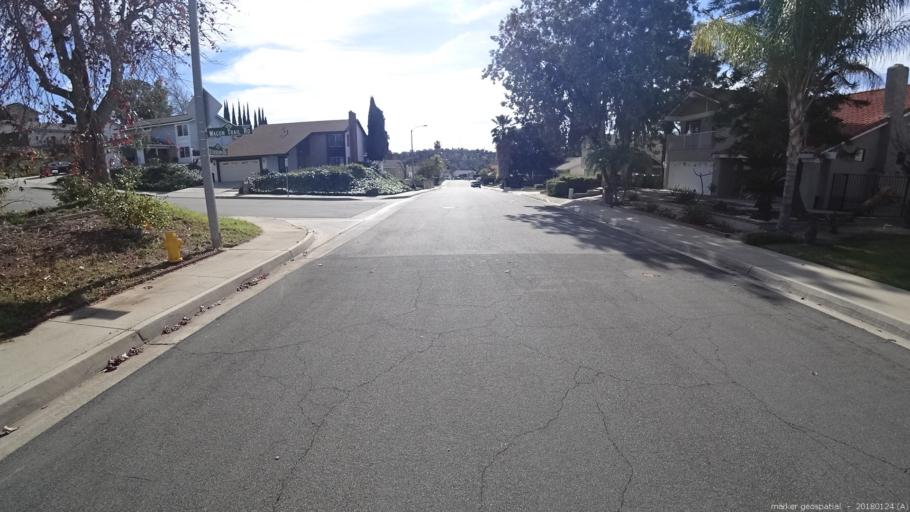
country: US
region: California
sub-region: Los Angeles County
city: Diamond Bar
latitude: 34.0141
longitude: -117.8106
